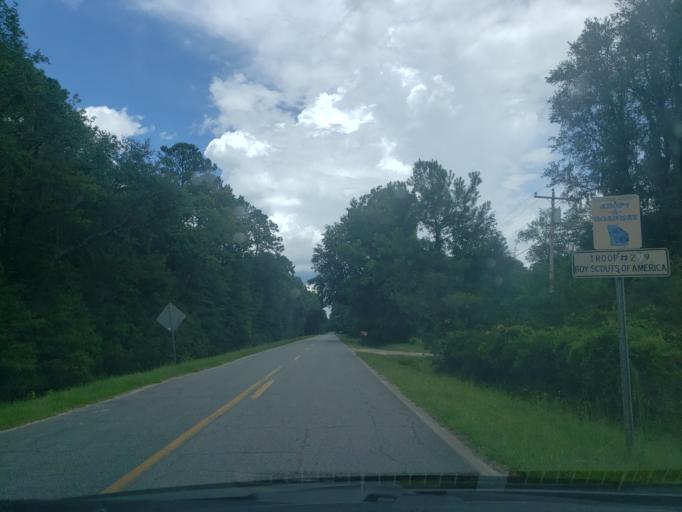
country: US
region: Georgia
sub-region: Bryan County
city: Richmond Hill
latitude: 32.0244
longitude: -81.3161
